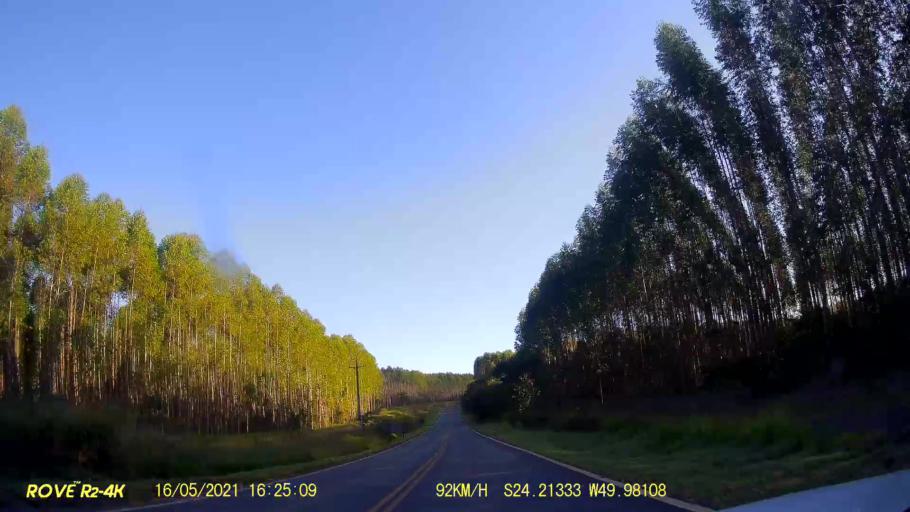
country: BR
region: Parana
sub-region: Jaguariaiva
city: Jaguariaiva
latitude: -24.2131
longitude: -49.9812
